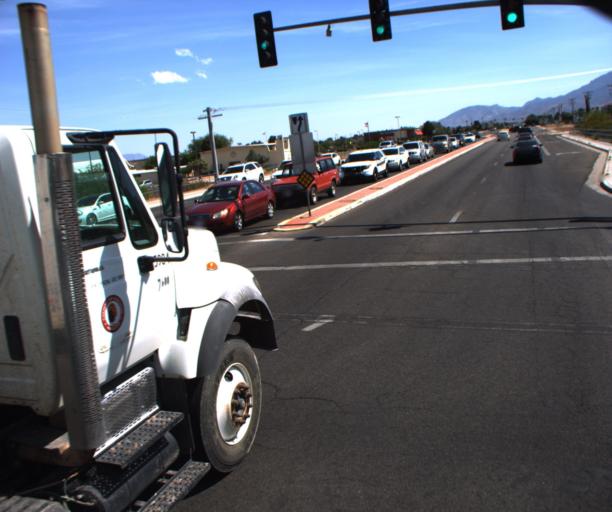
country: US
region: Arizona
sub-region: Cochise County
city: Sierra Vista
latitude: 31.5585
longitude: -110.2574
